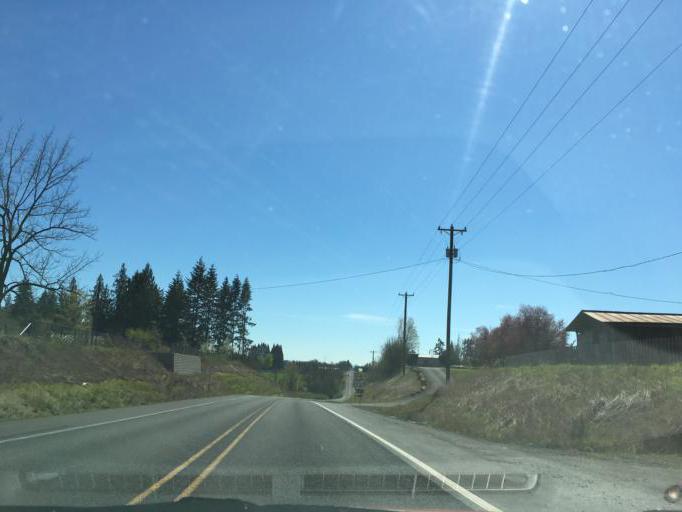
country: US
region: Oregon
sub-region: Clackamas County
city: Canby
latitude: 45.1968
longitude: -122.7227
